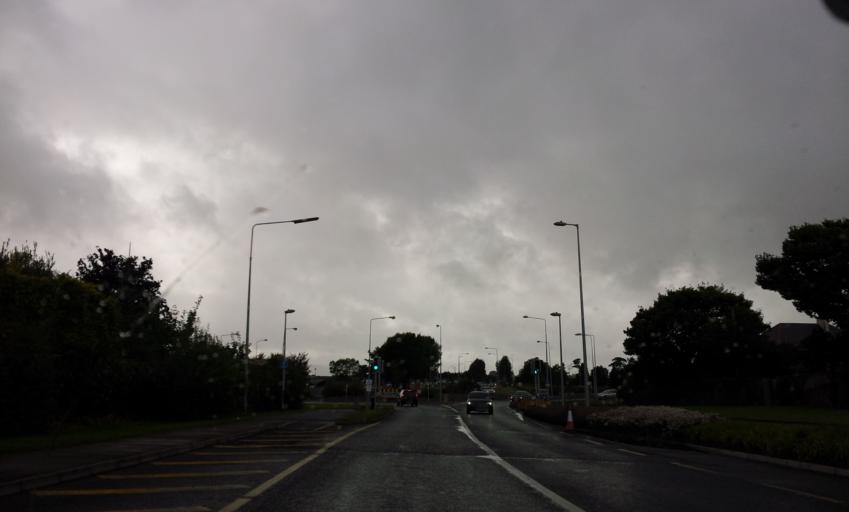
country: IE
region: Munster
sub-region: Waterford
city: Dungarvan
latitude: 52.0937
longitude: -7.6164
